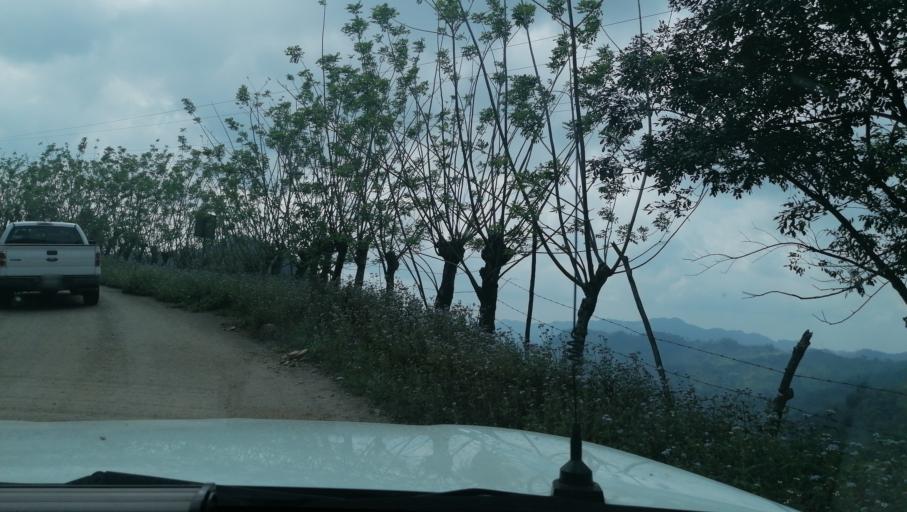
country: MX
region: Chiapas
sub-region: Francisco Leon
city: San Miguel la Sardina
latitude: 17.2491
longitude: -93.2836
